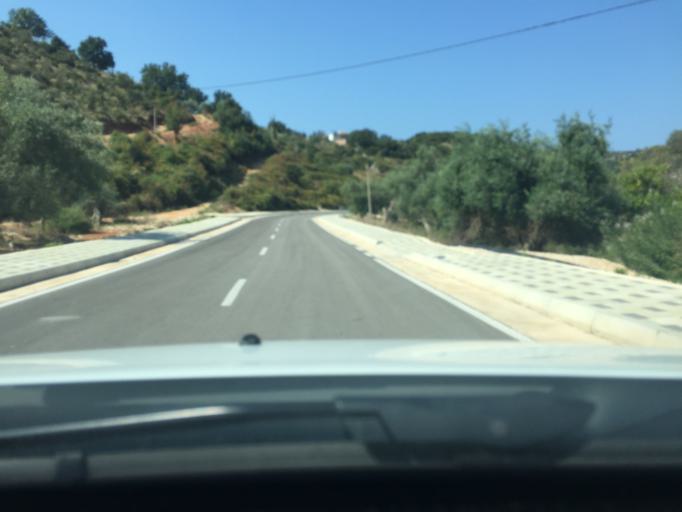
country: AL
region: Vlore
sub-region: Rrethi i Vlores
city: Himare
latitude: 40.1110
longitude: 19.7482
